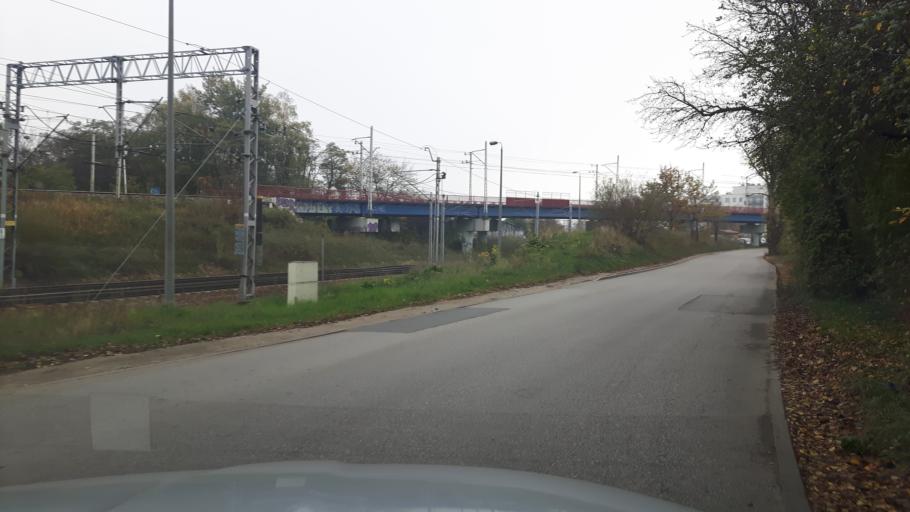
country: PL
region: Masovian Voivodeship
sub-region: Warszawa
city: Wlochy
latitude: 52.2035
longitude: 20.9431
